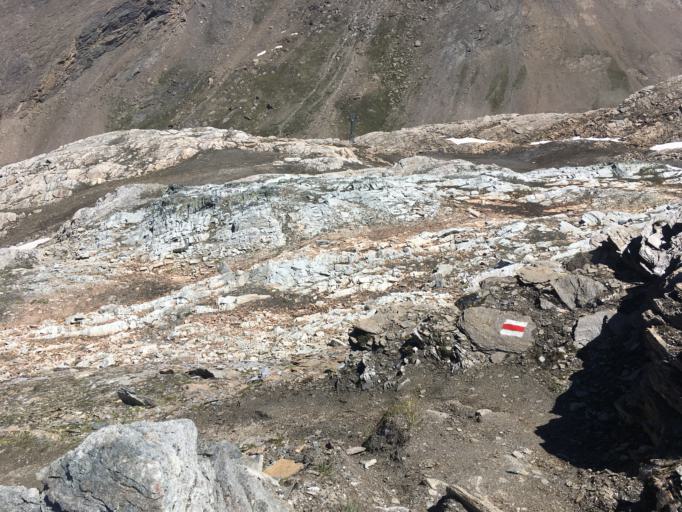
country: CH
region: Valais
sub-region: Visp District
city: Zermatt
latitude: 46.0247
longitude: 7.7952
